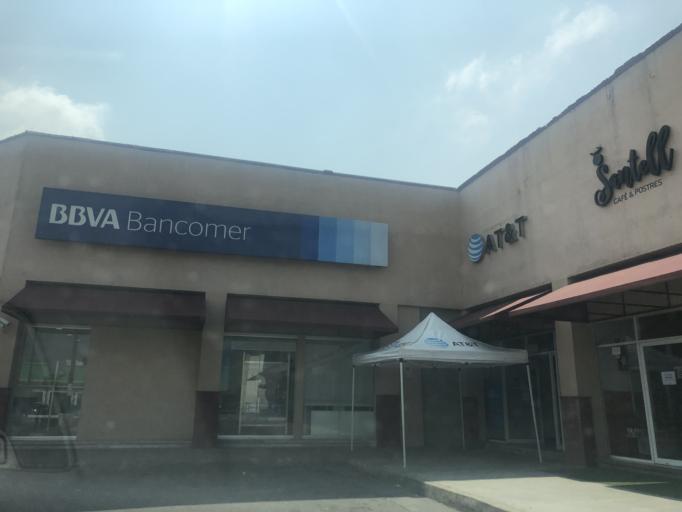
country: MX
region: Chiapas
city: San Cristobal de las Casas
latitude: 16.7203
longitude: -92.6428
